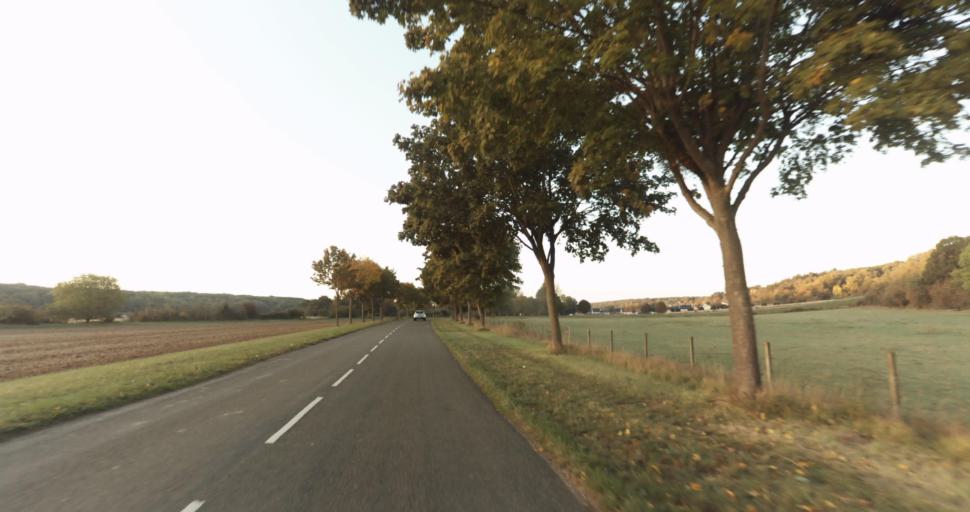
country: FR
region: Centre
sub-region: Departement d'Eure-et-Loir
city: Garnay
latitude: 48.7129
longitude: 1.3438
